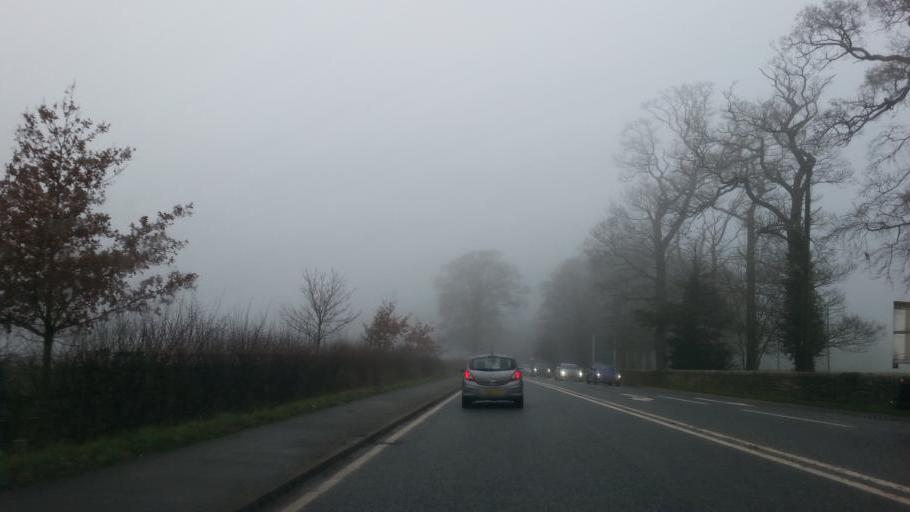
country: GB
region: England
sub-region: Cheshire East
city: Siddington
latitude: 53.2677
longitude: -2.2358
